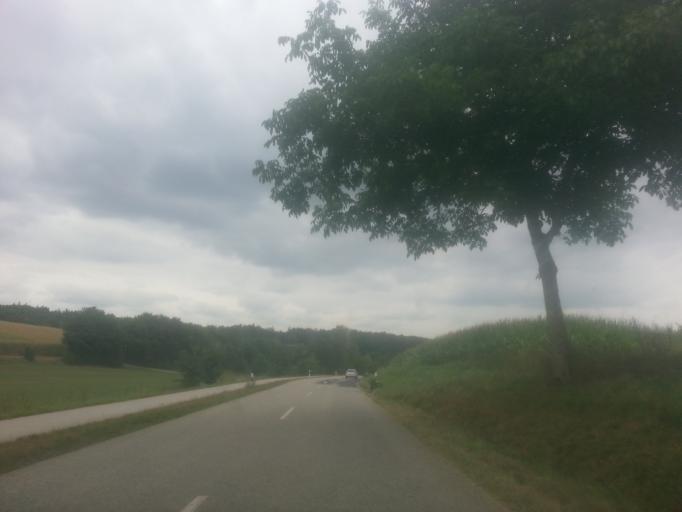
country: DE
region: Bavaria
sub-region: Lower Bavaria
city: Pfeffenhausen
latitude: 48.6728
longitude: 11.9329
